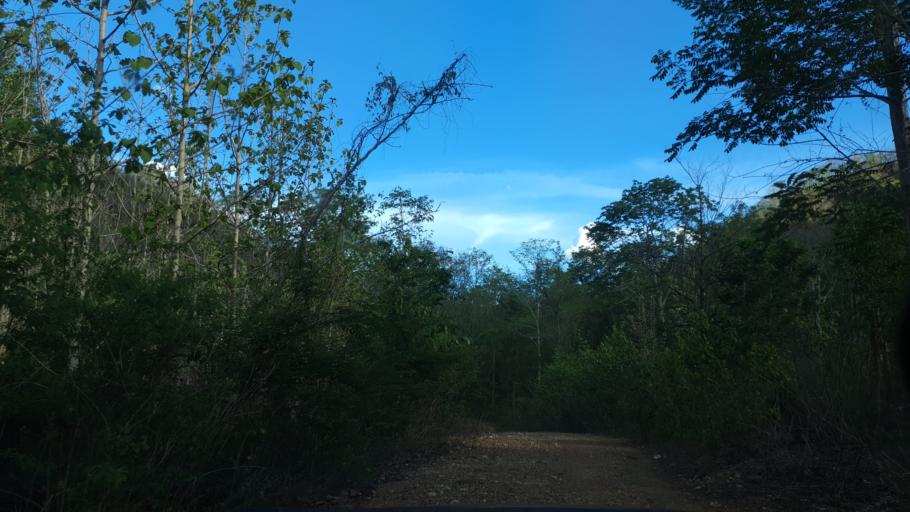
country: TH
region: Lampang
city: Sop Prap
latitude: 17.8469
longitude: 99.2853
